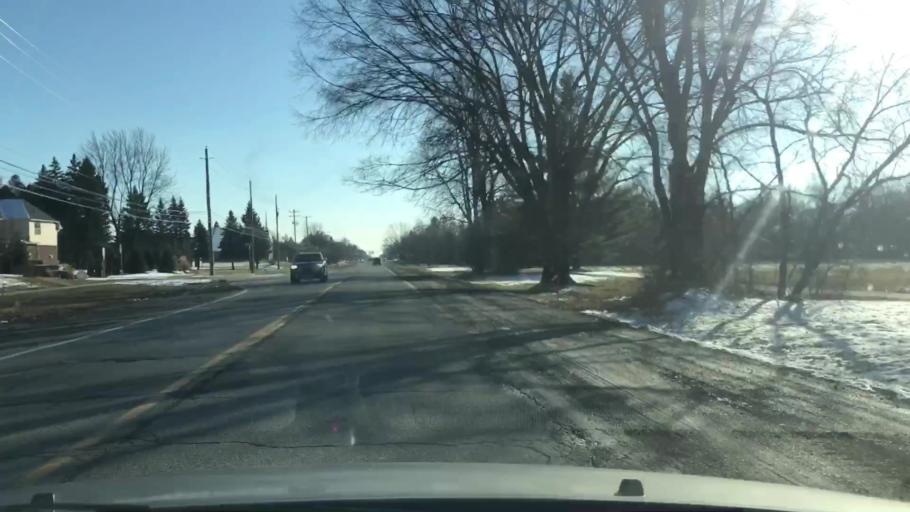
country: US
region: Michigan
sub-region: Oakland County
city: Troy
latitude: 42.5978
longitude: -83.1097
